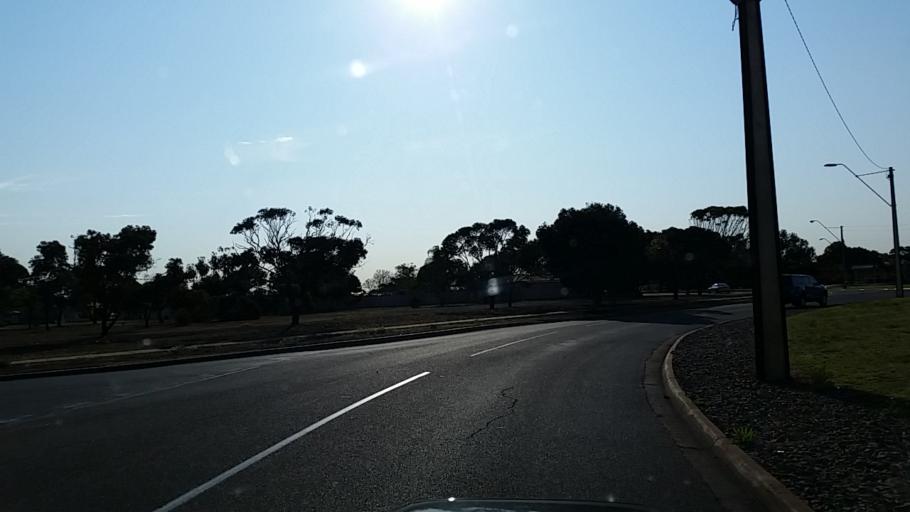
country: AU
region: South Australia
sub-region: Whyalla
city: Whyalla
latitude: -33.0264
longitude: 137.5306
